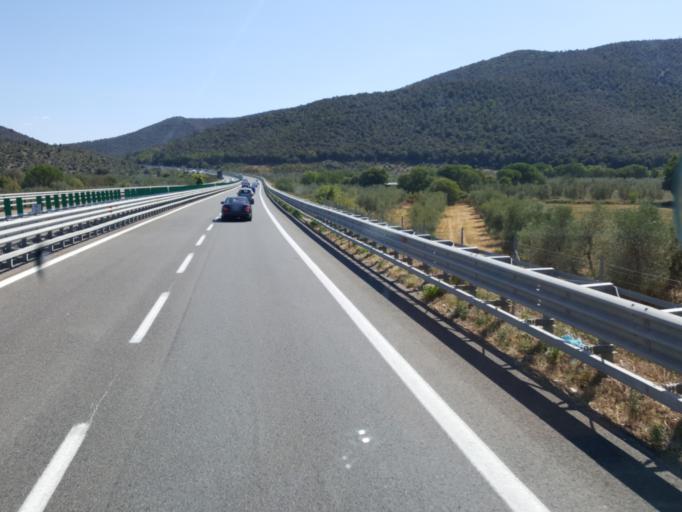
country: IT
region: Tuscany
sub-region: Provincia di Grosseto
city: Bagno Roselle
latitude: 42.8533
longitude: 11.1667
